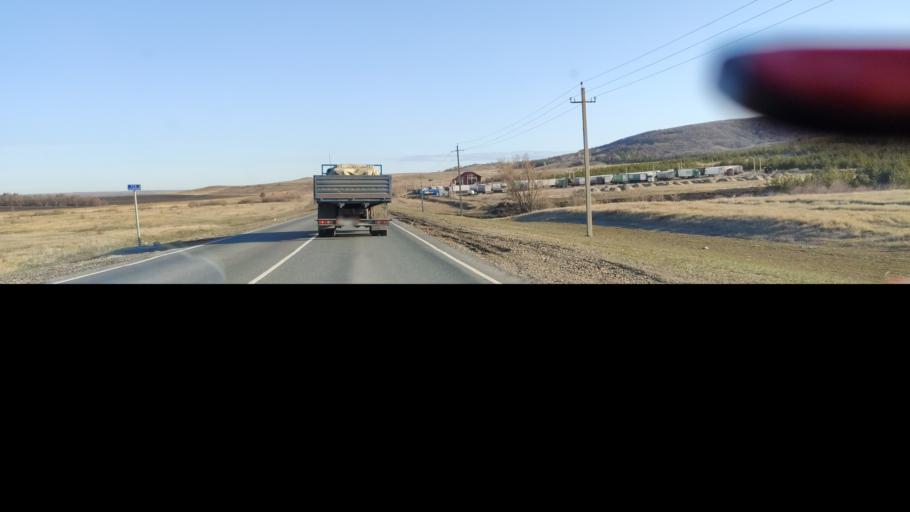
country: RU
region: Saratov
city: Alekseyevka
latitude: 52.3058
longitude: 47.9257
